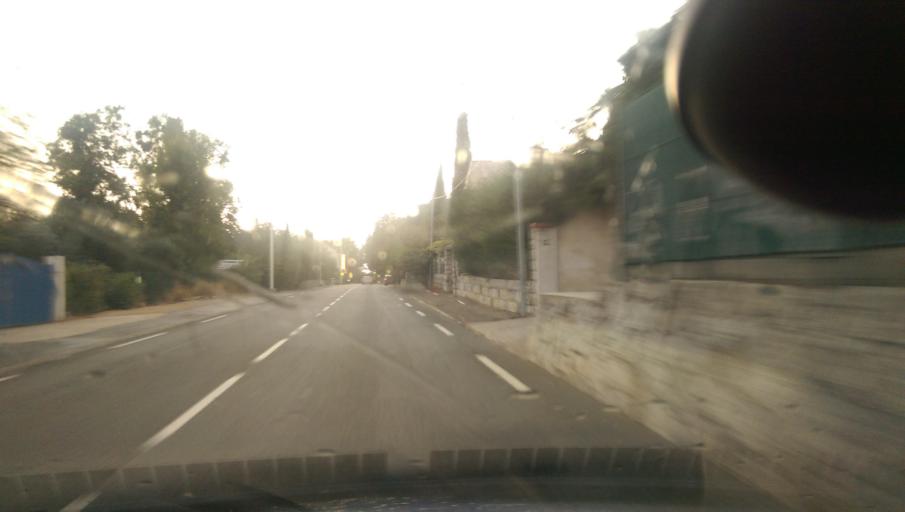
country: FR
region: Provence-Alpes-Cote d'Azur
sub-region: Departement des Alpes-Maritimes
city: Grasse
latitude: 43.6786
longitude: 6.9476
